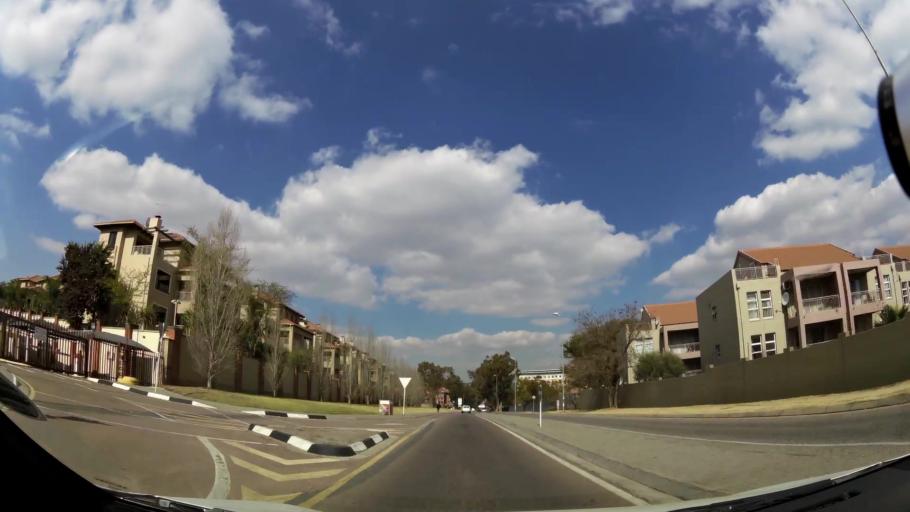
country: ZA
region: Gauteng
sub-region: City of Johannesburg Metropolitan Municipality
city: Midrand
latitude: -26.0335
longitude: 28.0642
